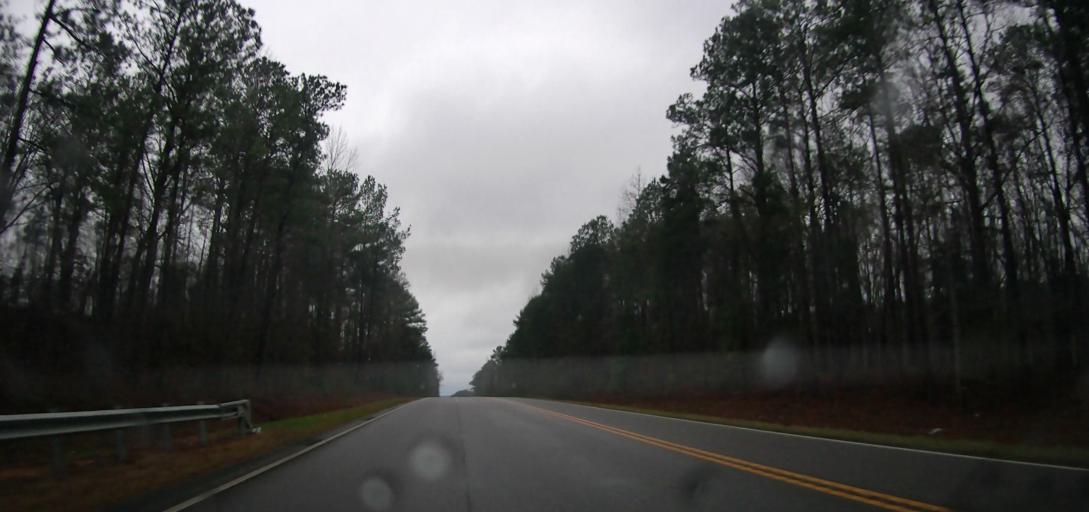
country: US
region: Alabama
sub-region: Bibb County
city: West Blocton
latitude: 33.0346
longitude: -87.1402
